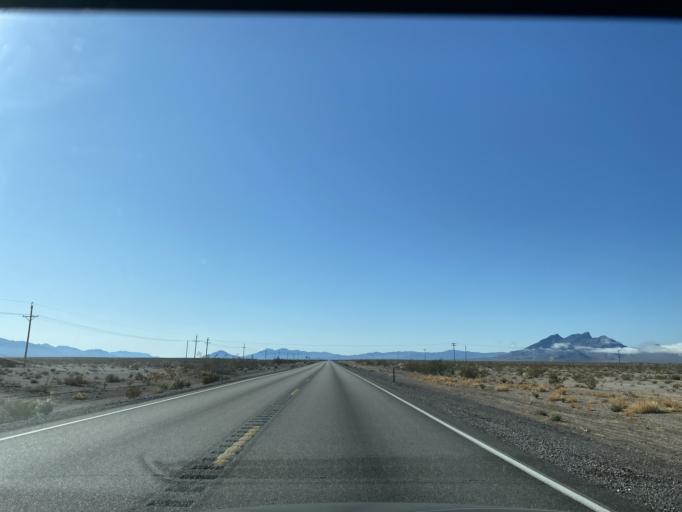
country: US
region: Nevada
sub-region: Nye County
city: Pahrump
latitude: 36.4836
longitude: -116.4215
